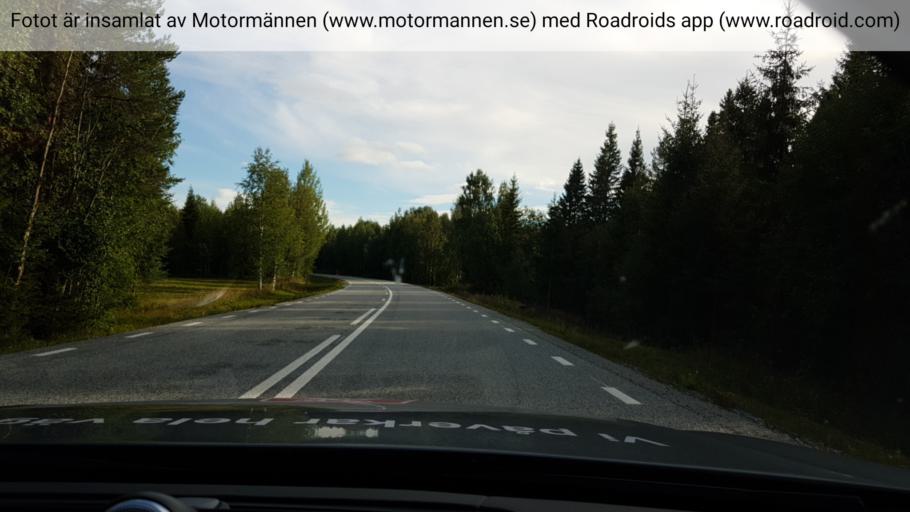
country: SE
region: Jaemtland
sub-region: Stroemsunds Kommun
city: Stroemsund
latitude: 64.1599
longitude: 15.6757
